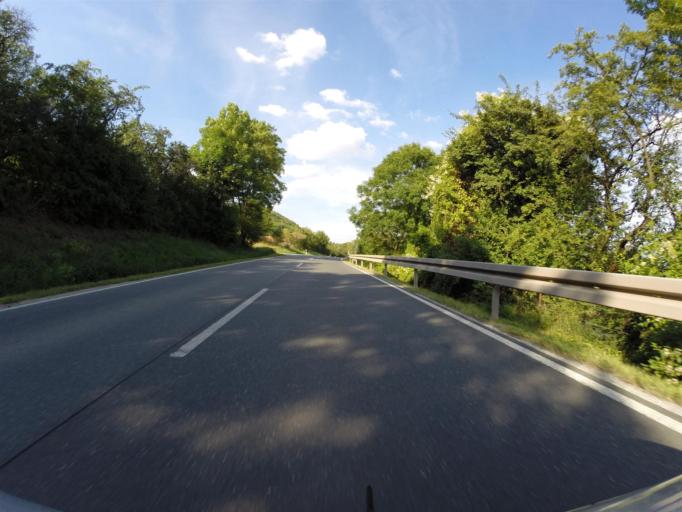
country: DE
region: Thuringia
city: Neuengonna
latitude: 50.9744
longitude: 11.6378
